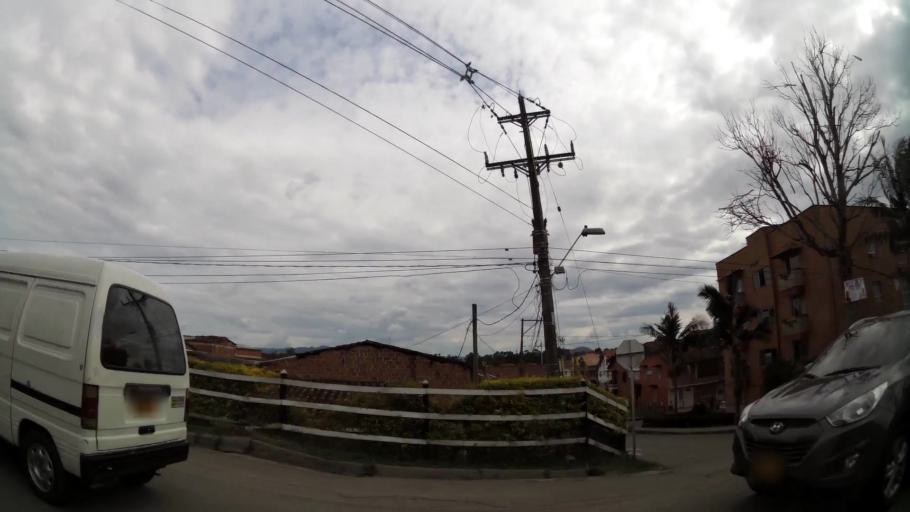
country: CO
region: Antioquia
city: Rionegro
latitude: 6.1503
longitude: -75.3880
